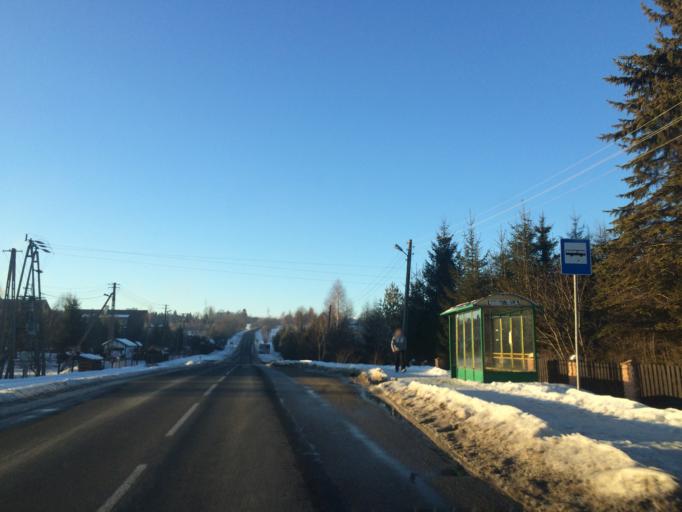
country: PL
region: Subcarpathian Voivodeship
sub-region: Powiat bieszczadzki
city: Lutowiska
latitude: 49.2550
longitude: 22.6895
